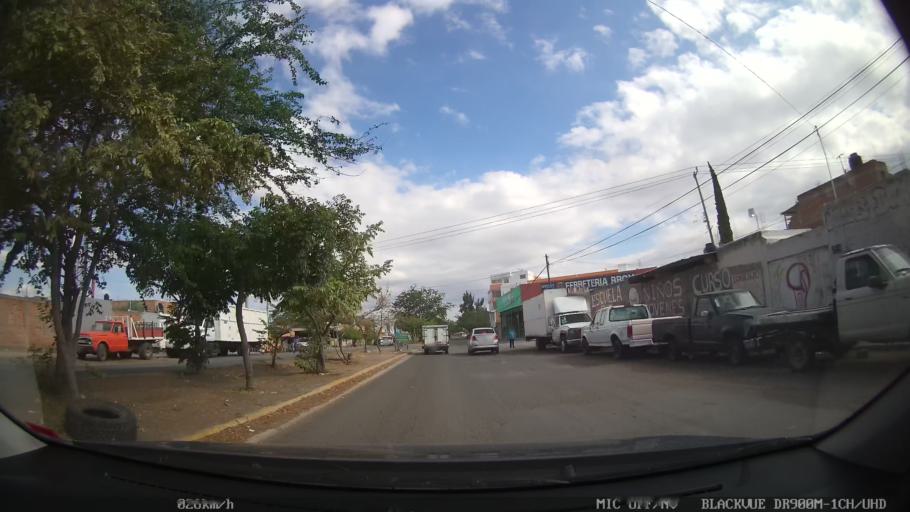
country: MX
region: Jalisco
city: Tlaquepaque
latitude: 20.6685
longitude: -103.2549
